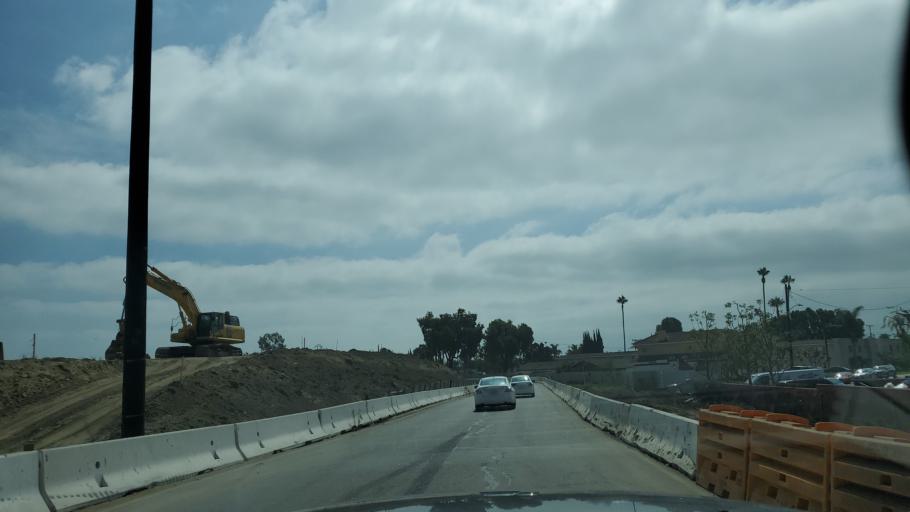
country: US
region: California
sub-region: Orange County
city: Westminster
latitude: 33.7588
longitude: -118.0238
